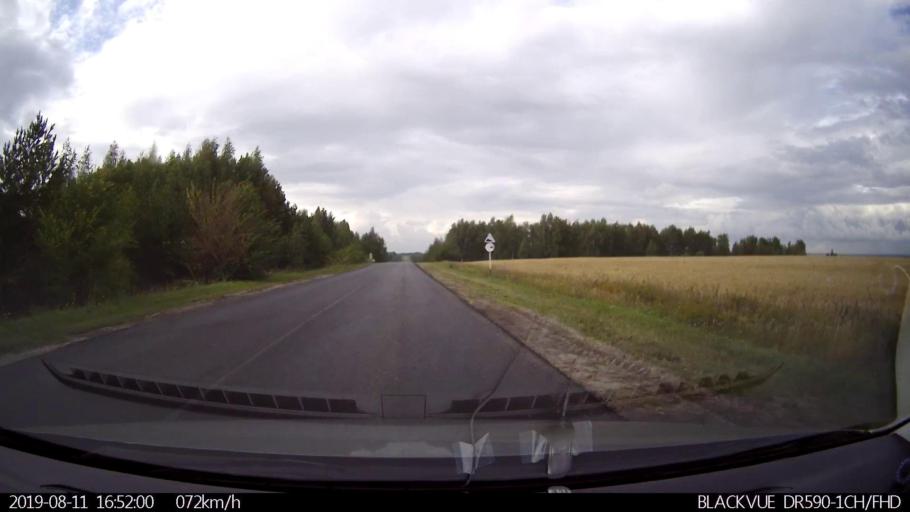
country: RU
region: Ulyanovsk
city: Mayna
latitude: 54.2430
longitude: 47.6755
